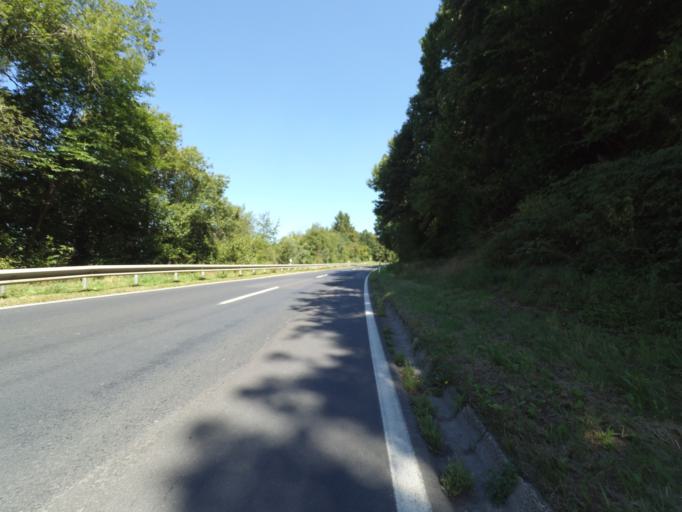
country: DE
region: Rheinland-Pfalz
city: Mullenbach
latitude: 50.2137
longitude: 7.0574
